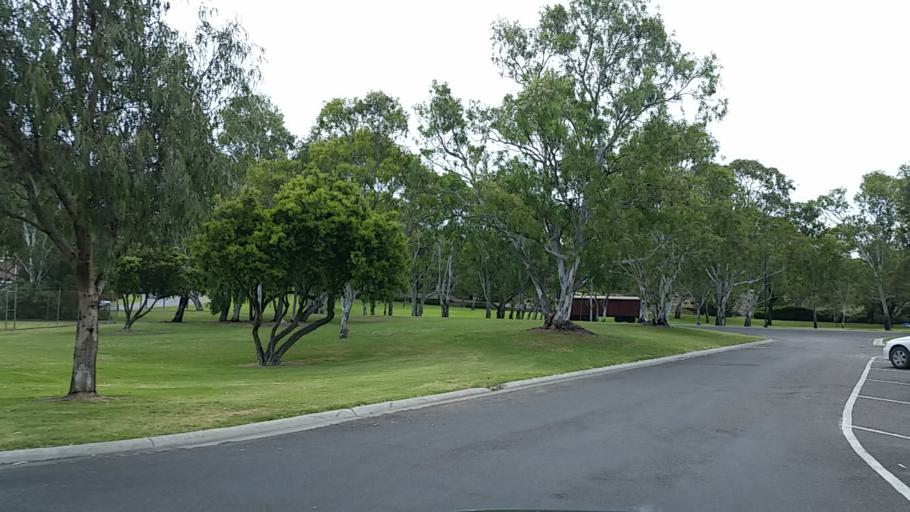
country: AU
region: South Australia
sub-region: Murray Bridge
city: Murray Bridge
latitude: -35.1187
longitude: 139.2814
